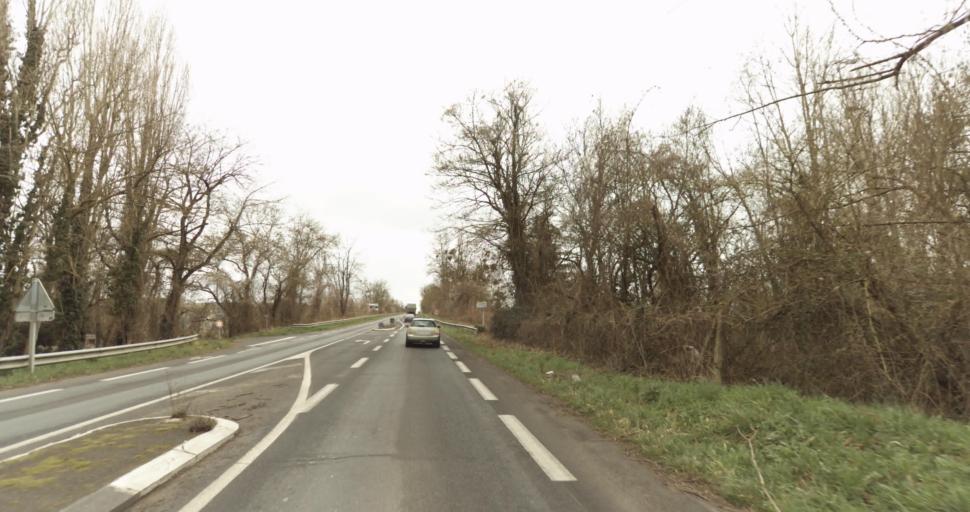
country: FR
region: Pays de la Loire
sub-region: Departement de Maine-et-Loire
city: Varrains
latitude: 47.2374
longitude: -0.0777
